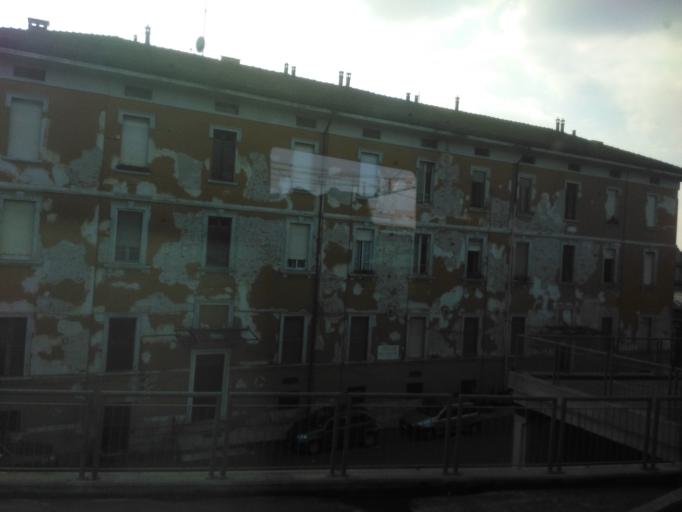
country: IT
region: Lombardy
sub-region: Citta metropolitana di Milano
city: Sesto San Giovanni
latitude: 45.4991
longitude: 9.2187
